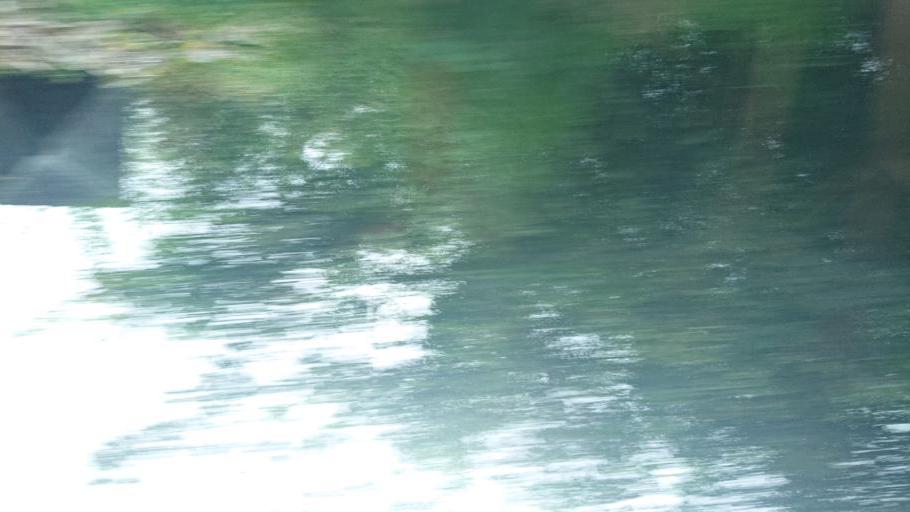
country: TW
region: Taiwan
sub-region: Chiayi
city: Jiayi Shi
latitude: 23.4715
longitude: 120.7056
